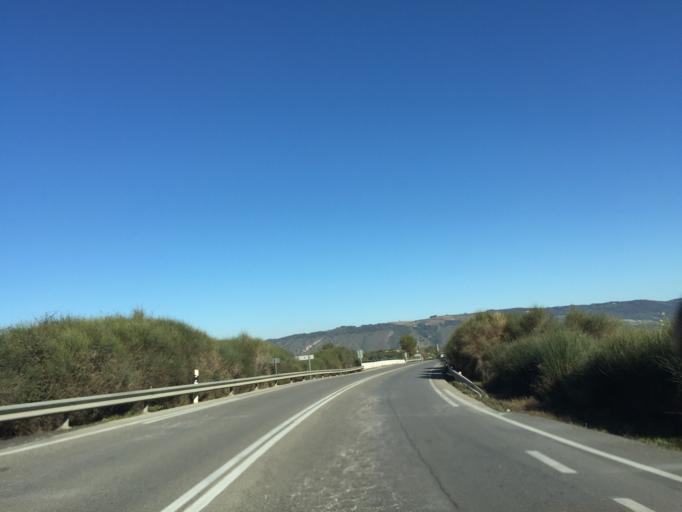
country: ES
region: Andalusia
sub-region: Provincia de Malaga
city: Ronda
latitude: 36.7557
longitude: -5.1546
